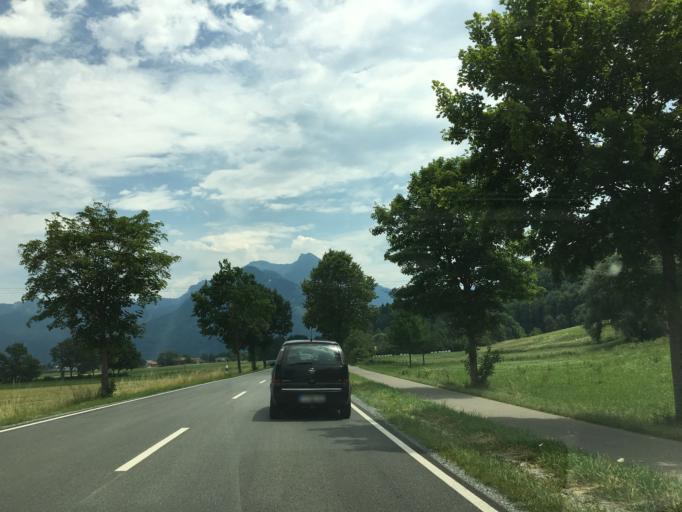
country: DE
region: Bavaria
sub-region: Upper Bavaria
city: Grassau
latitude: 47.7828
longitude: 12.4329
